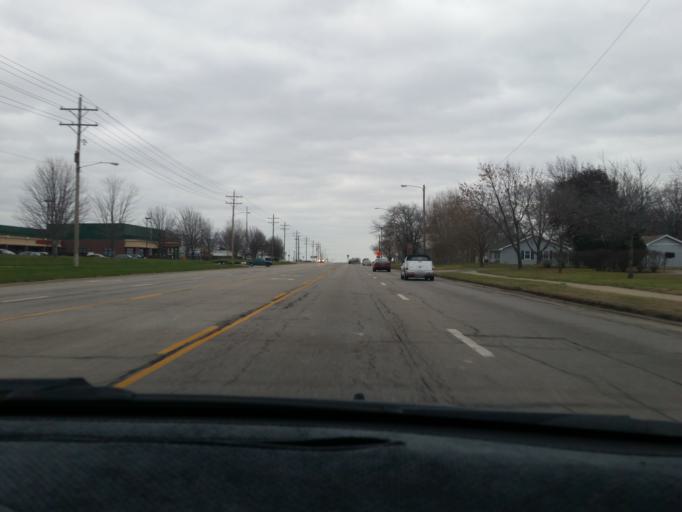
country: US
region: Kansas
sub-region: Douglas County
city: Lawrence
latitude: 38.9427
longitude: -95.2131
